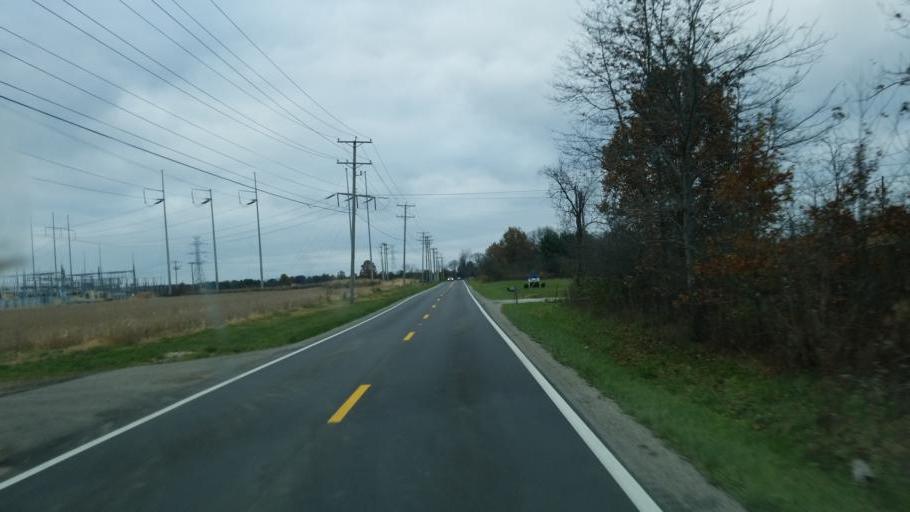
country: US
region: Ohio
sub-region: Franklin County
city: New Albany
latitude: 40.1220
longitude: -82.8412
